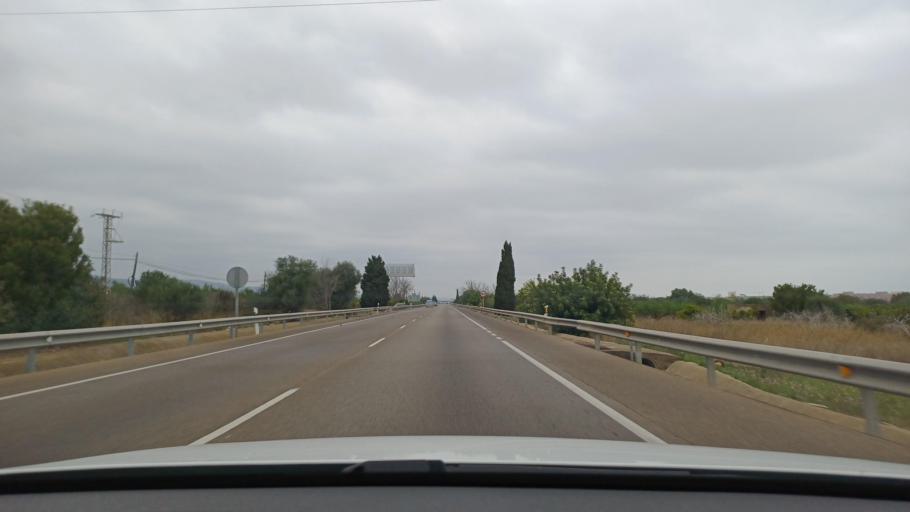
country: ES
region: Valencia
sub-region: Provincia de Castello
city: Orpesa/Oropesa del Mar
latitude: 40.1084
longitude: 0.1378
